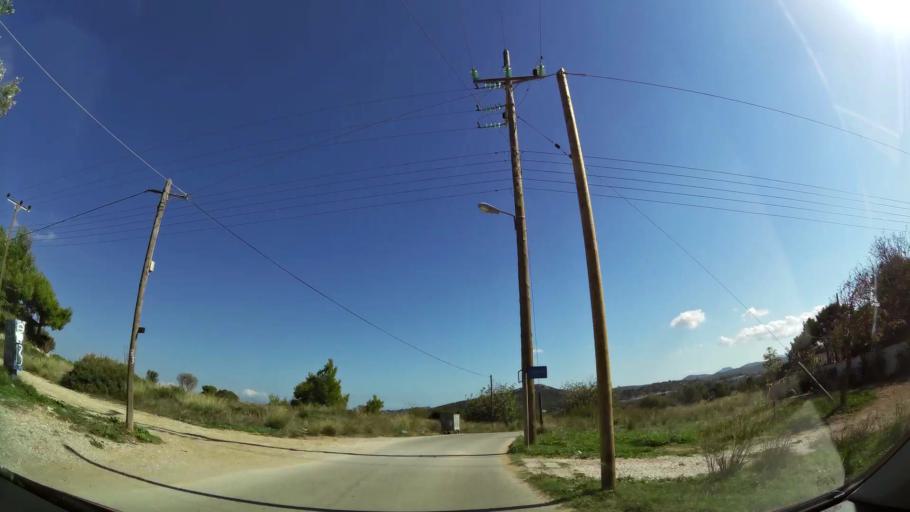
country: GR
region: Attica
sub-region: Nomarchia Anatolikis Attikis
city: Pikermi
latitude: 38.0109
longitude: 23.9391
